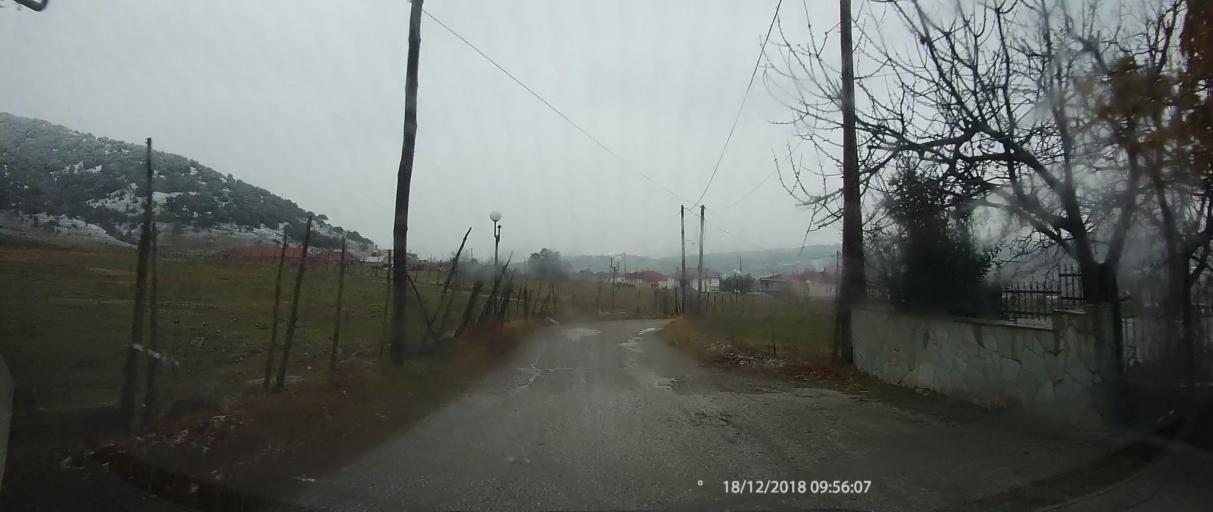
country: GR
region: Thessaly
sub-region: Nomos Larisis
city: Livadi
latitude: 40.0239
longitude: 22.2460
